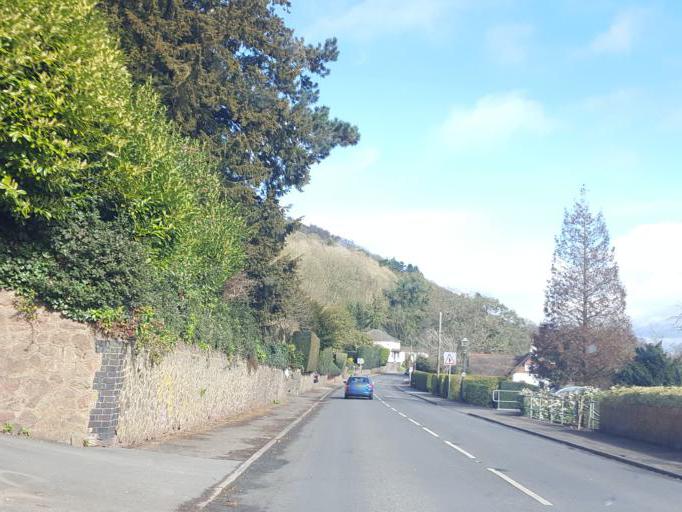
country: GB
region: England
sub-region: Worcestershire
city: Great Malvern
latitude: 52.0908
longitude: -2.3346
